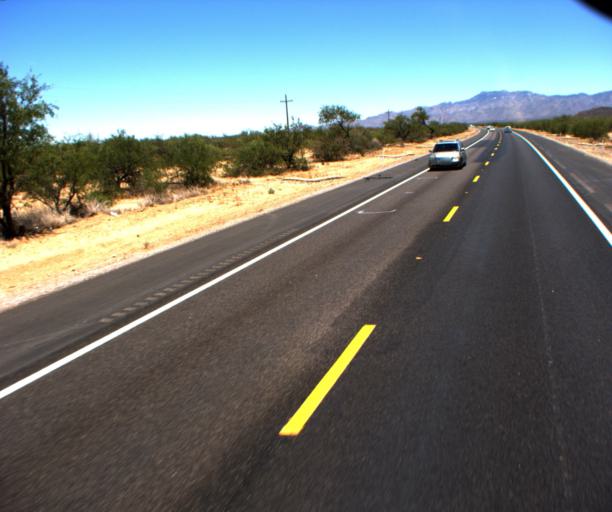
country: US
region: Arizona
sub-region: Pima County
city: Sells
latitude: 31.9196
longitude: -111.8303
